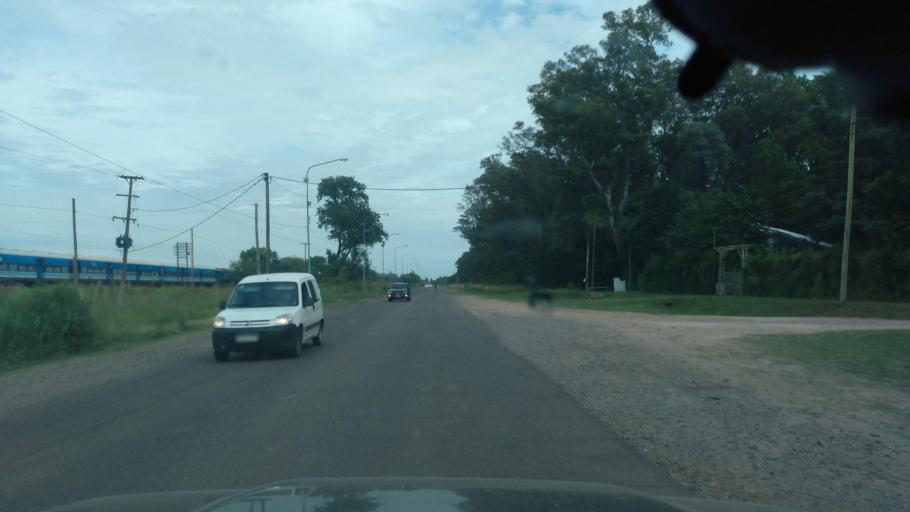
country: AR
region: Buenos Aires
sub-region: Partido de Lujan
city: Lujan
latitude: -34.5806
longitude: -59.0722
